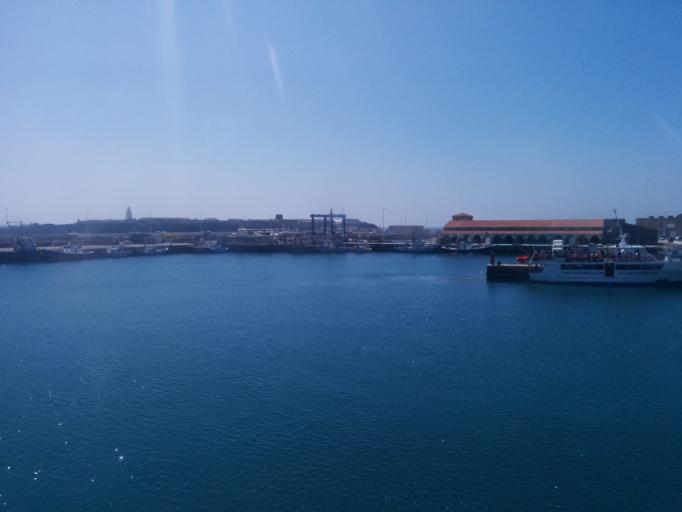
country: ES
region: Andalusia
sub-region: Provincia de Cadiz
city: Tarifa
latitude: 36.0098
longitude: -5.6034
